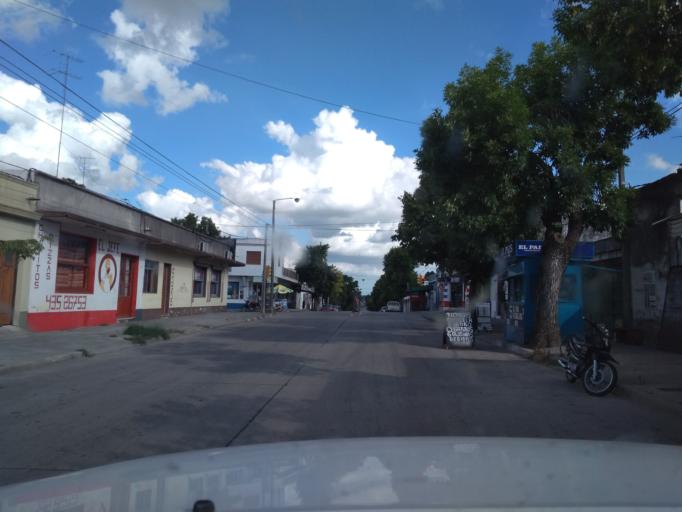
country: UY
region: Florida
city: Florida
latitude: -34.0948
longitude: -56.2122
